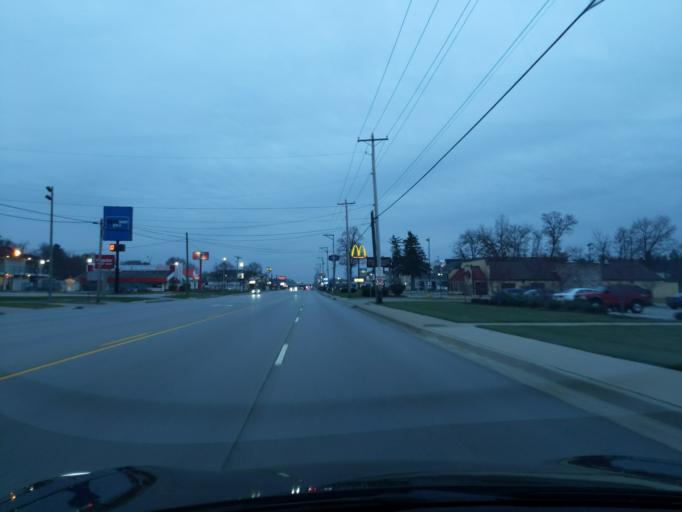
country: US
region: Indiana
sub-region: Saint Joseph County
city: Georgetown
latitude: 41.7293
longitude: -86.2508
